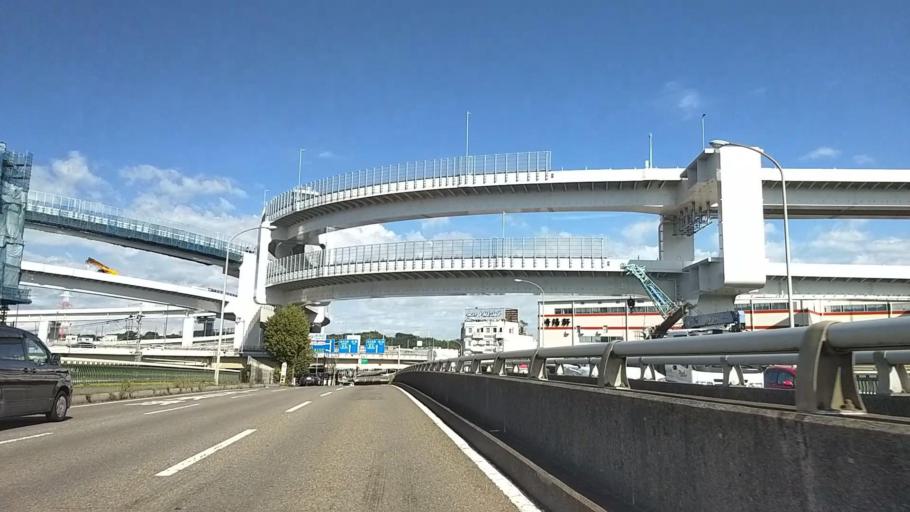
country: JP
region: Kanagawa
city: Yokohama
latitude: 35.5163
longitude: 139.5945
